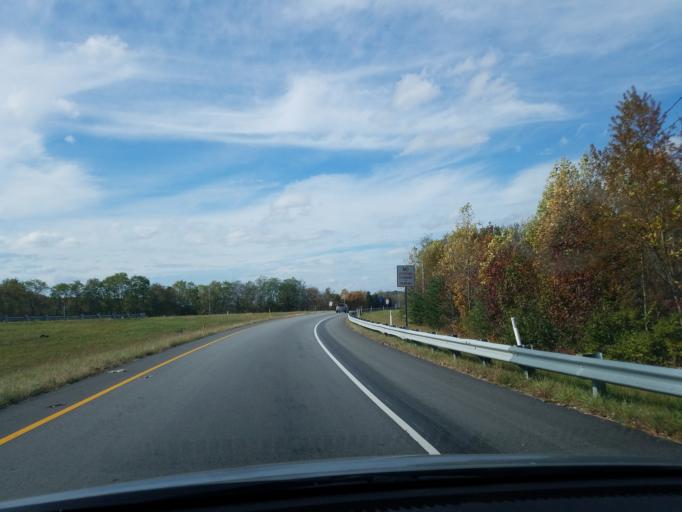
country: US
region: Indiana
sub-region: Floyd County
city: New Albany
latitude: 38.3042
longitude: -85.8901
